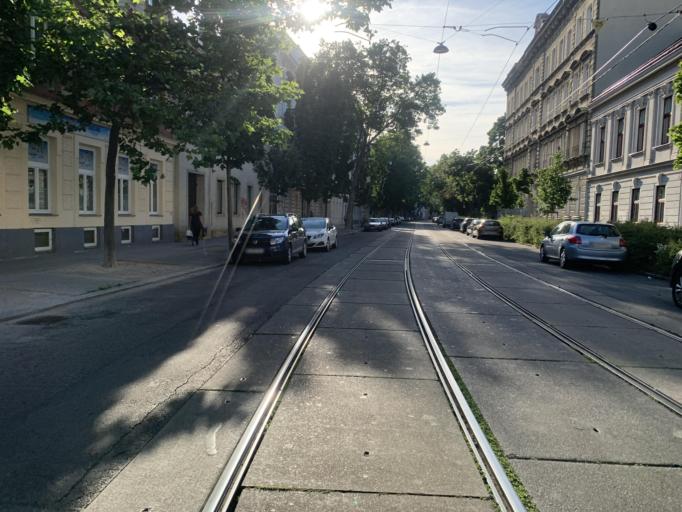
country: AT
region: Vienna
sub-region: Wien Stadt
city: Vienna
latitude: 48.2553
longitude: 16.4060
